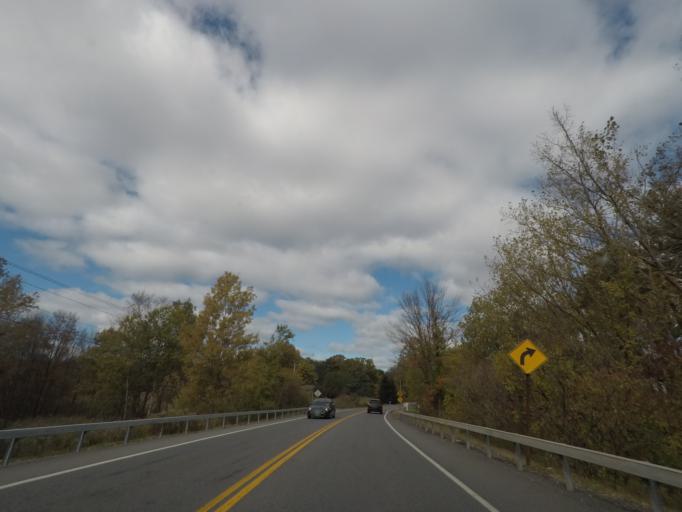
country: US
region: New York
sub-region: Saratoga County
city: Country Knolls
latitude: 42.8406
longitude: -73.7689
